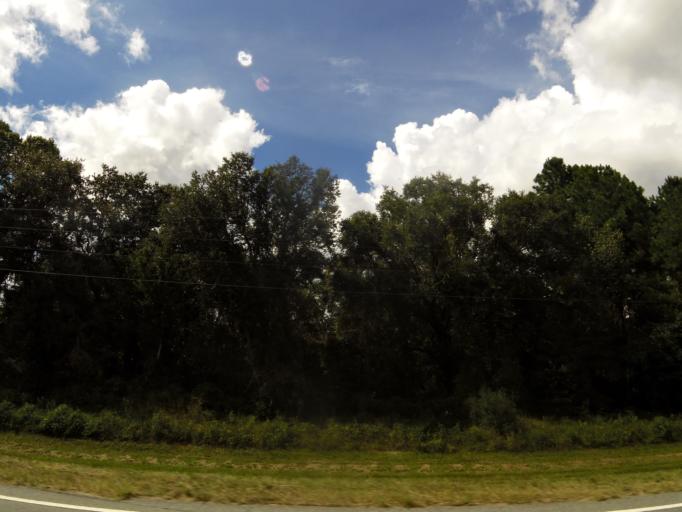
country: US
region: Georgia
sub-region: Brantley County
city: Nahunta
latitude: 31.1151
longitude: -82.0035
